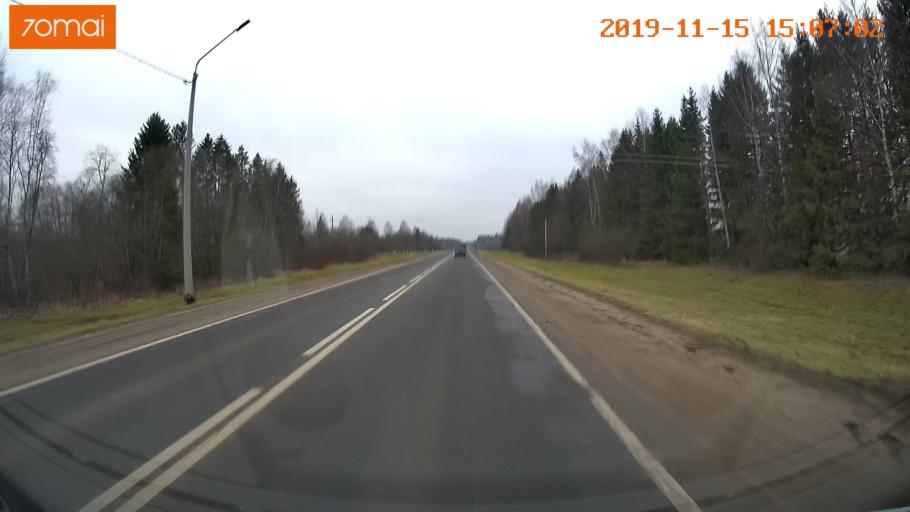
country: RU
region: Jaroslavl
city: Prechistoye
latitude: 58.3877
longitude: 40.3023
